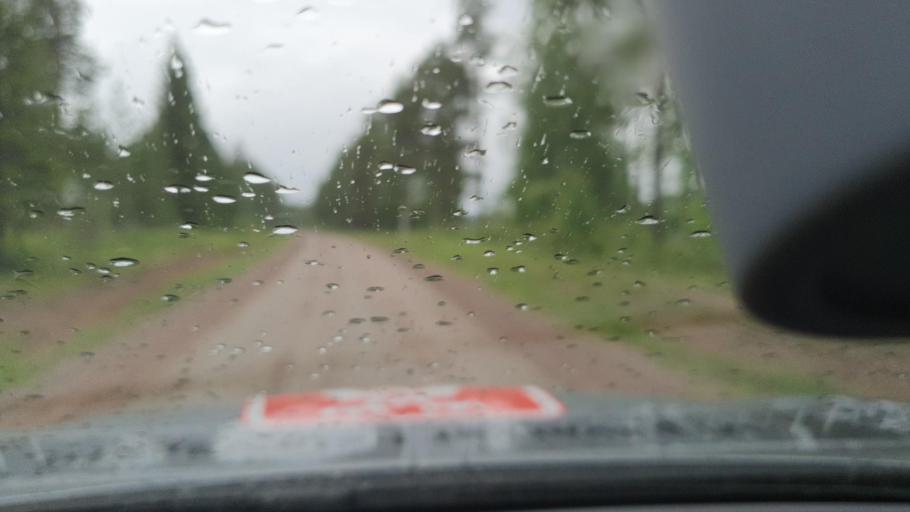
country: SE
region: Norrbotten
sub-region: Overkalix Kommun
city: OEverkalix
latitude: 66.4984
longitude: 22.7612
